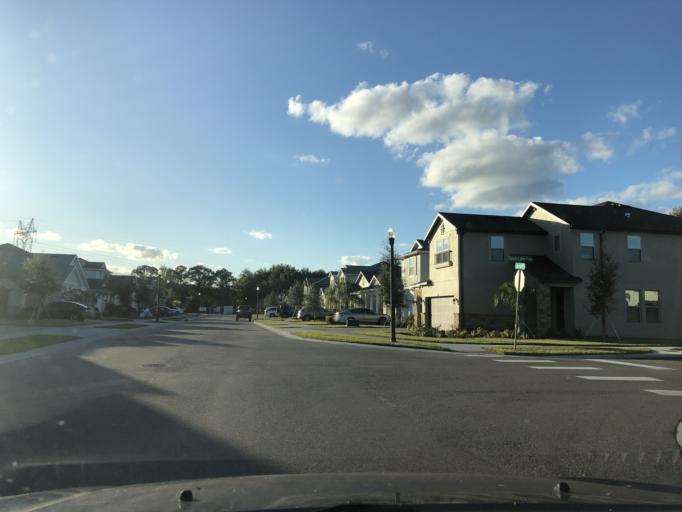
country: US
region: Florida
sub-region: Seminole County
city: Goldenrod
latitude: 28.6120
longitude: -81.2619
